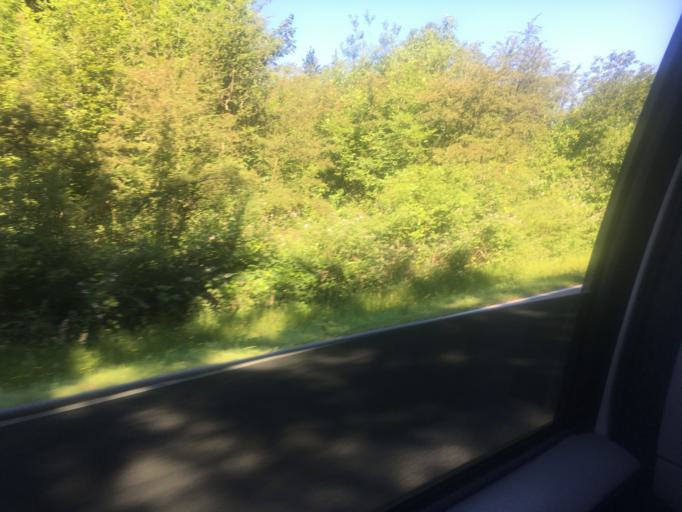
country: US
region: Washington
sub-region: King County
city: Bellevue
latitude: 47.6113
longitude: -122.1749
